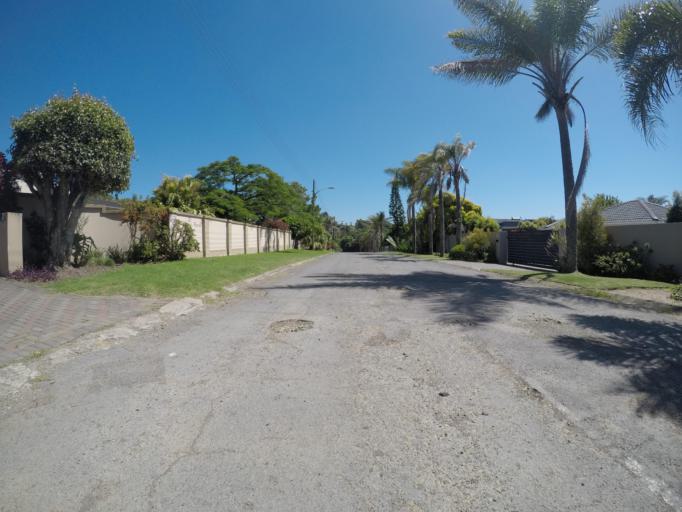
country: ZA
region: Eastern Cape
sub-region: Buffalo City Metropolitan Municipality
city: East London
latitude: -32.9728
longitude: 27.9438
